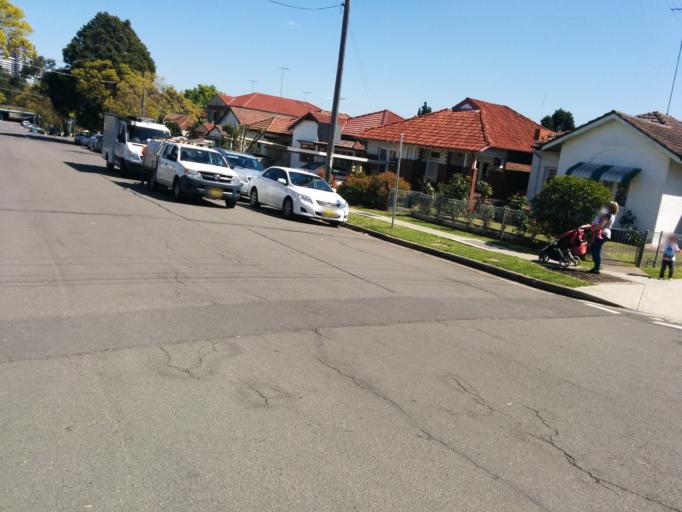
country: AU
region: New South Wales
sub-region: Canada Bay
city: Concord West
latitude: -33.8479
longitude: 151.0850
